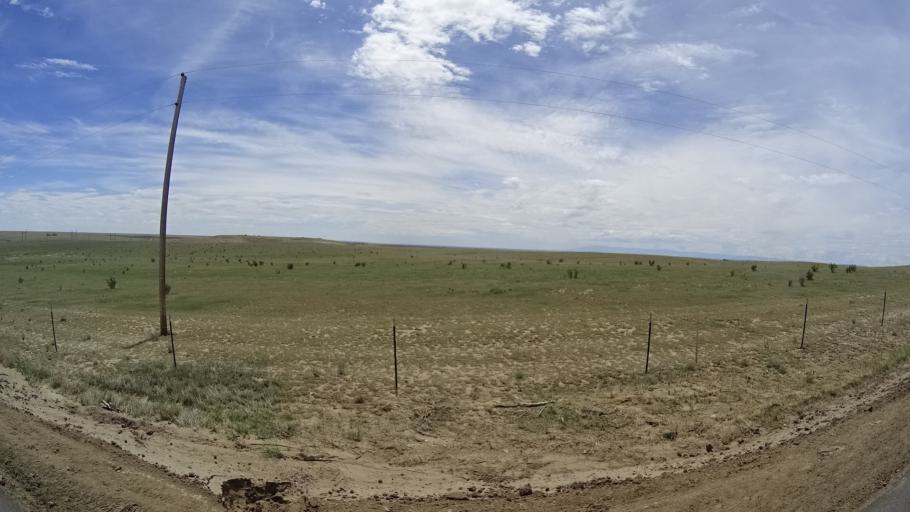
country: US
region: Colorado
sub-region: El Paso County
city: Fountain
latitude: 38.6940
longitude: -104.6416
